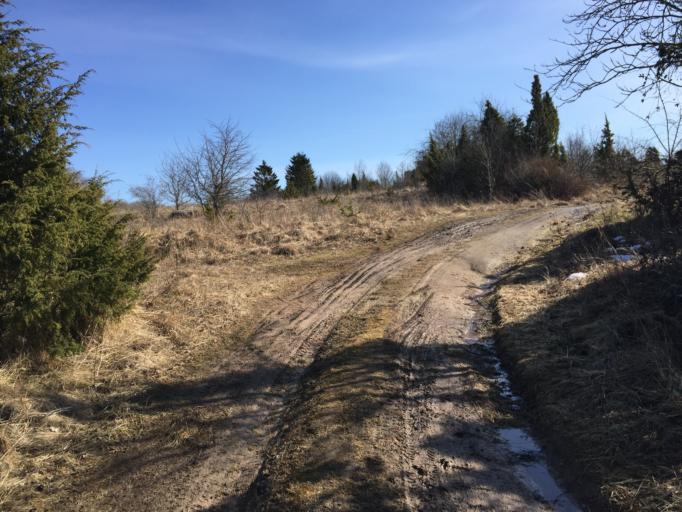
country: EE
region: Laeaene
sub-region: Haapsalu linn
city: Haapsalu
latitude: 58.6466
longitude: 23.5122
